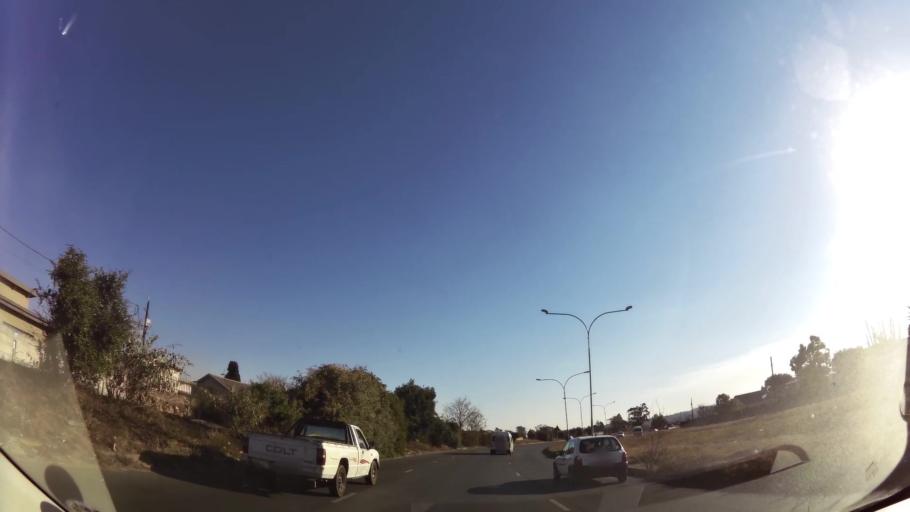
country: ZA
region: Gauteng
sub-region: City of Johannesburg Metropolitan Municipality
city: Johannesburg
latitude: -26.2067
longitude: 27.9631
